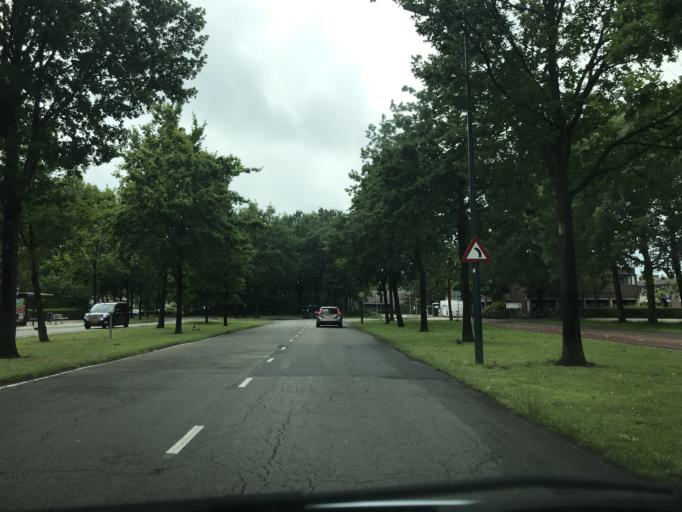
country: NL
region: North Brabant
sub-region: Gemeente Breda
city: Breda
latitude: 51.5714
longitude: 4.7681
